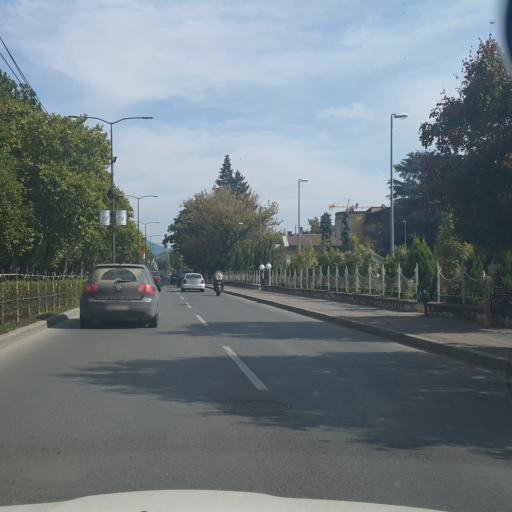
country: RS
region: Central Serbia
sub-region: Nisavski Okrug
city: Nis
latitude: 43.3172
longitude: 21.9124
